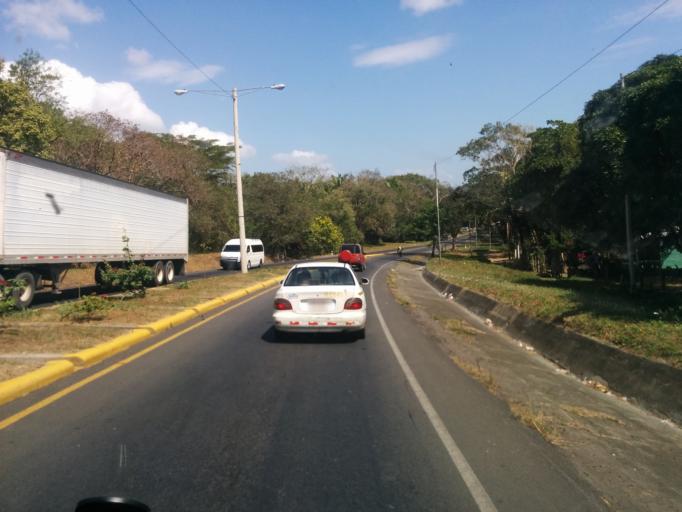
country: NI
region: Masaya
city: Masaya
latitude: 11.9574
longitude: -86.0909
